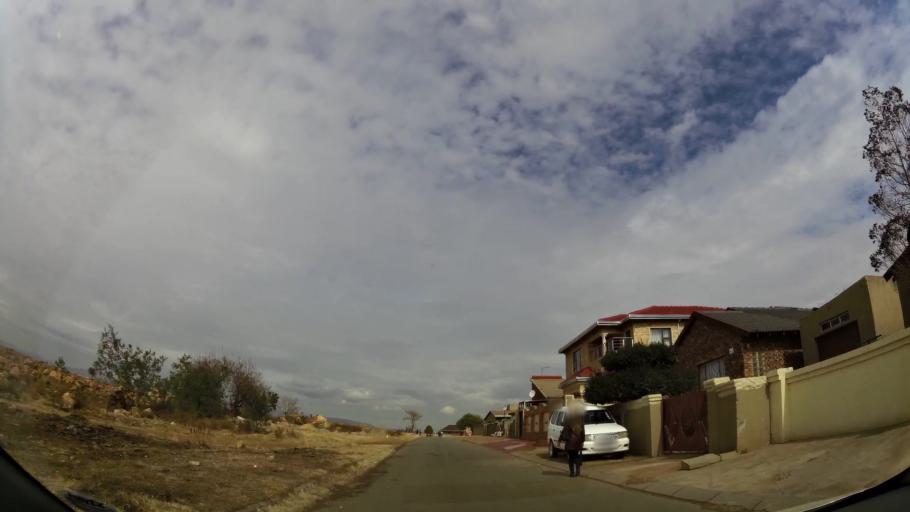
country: ZA
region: Gauteng
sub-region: Ekurhuleni Metropolitan Municipality
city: Germiston
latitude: -26.3792
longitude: 28.1686
